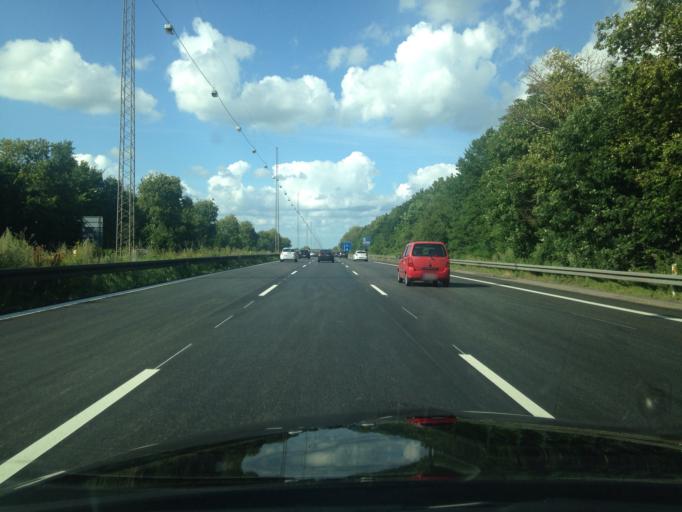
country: DK
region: Capital Region
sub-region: Lyngby-Tarbaek Kommune
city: Kongens Lyngby
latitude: 55.7812
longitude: 12.5269
